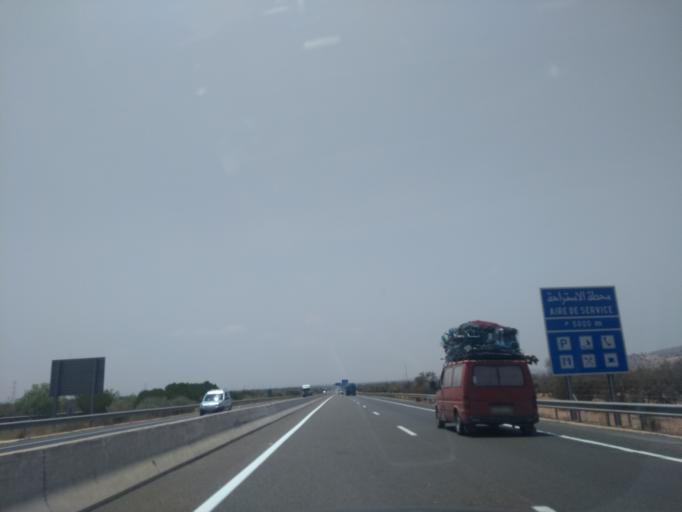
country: MA
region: Souss-Massa-Draa
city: Oulad Teima
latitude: 30.4952
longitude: -9.3380
